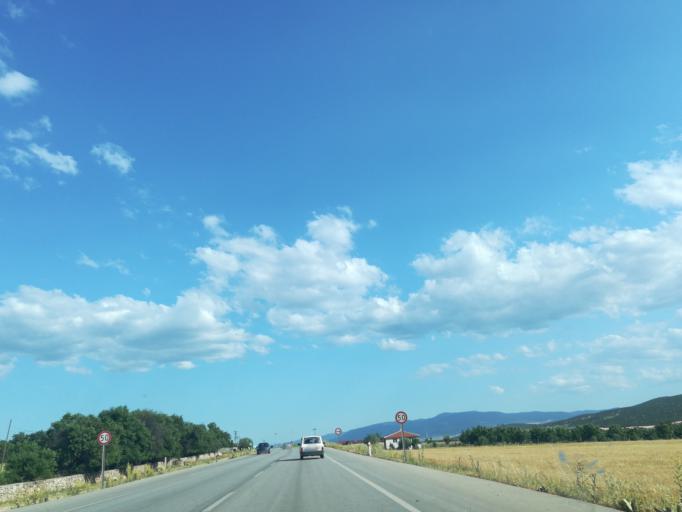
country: TR
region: Afyonkarahisar
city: Dinar
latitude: 38.1315
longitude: 30.1010
